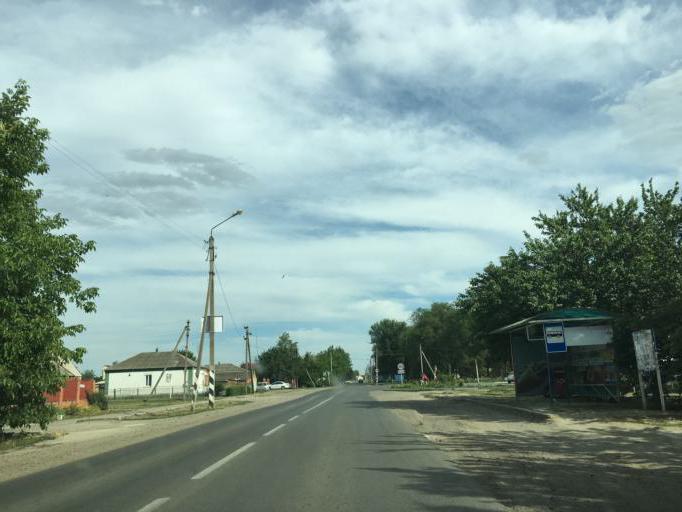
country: RU
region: Krasnodarskiy
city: Kushchevskaya
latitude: 46.5447
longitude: 39.6213
